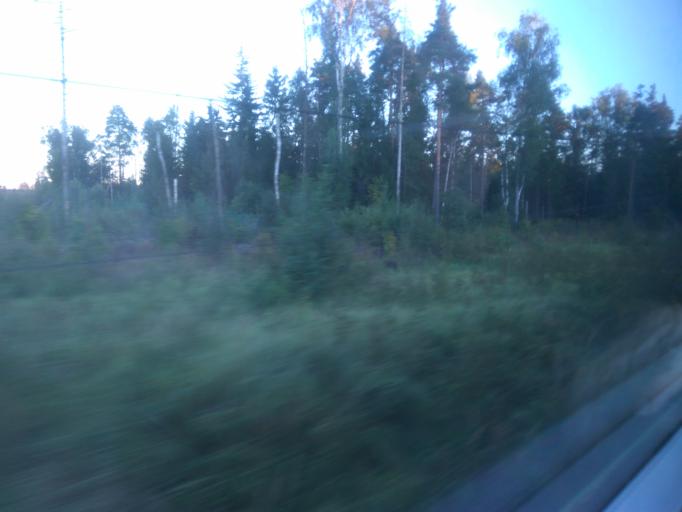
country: RU
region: Moskovskaya
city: Fryazevo
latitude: 55.7397
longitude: 38.4791
